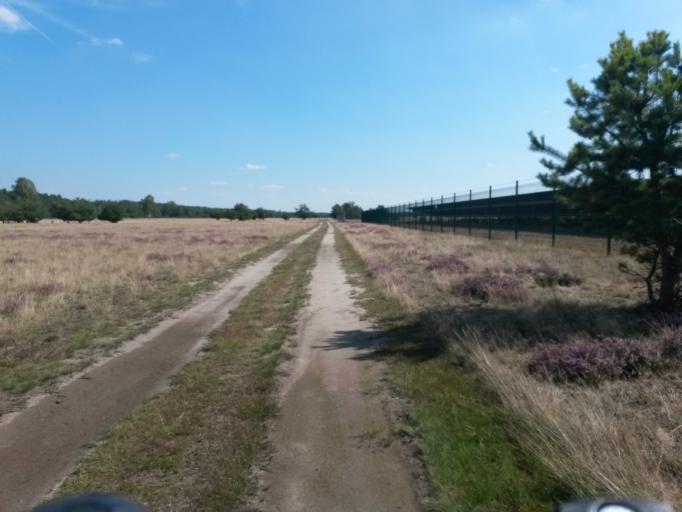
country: DE
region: Brandenburg
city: Templin
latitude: 53.0330
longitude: 13.5526
